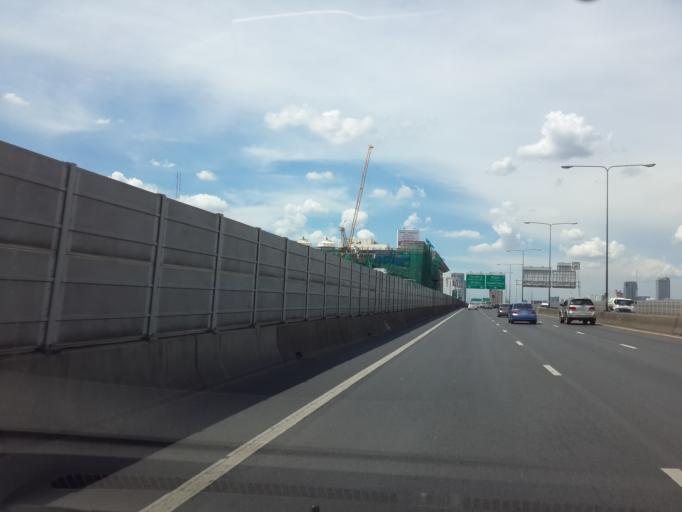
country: TH
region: Bangkok
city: Ratchathewi
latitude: 13.7660
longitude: 100.5274
